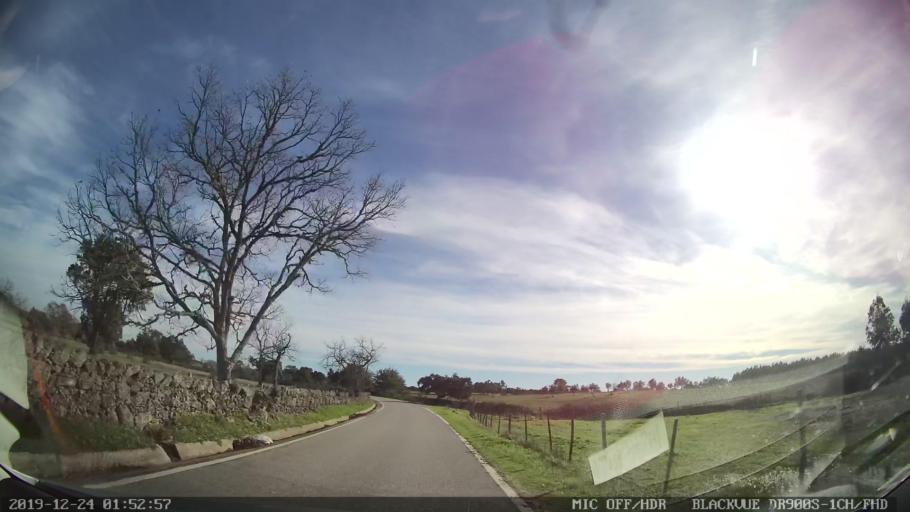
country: PT
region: Portalegre
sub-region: Nisa
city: Nisa
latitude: 39.4885
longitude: -7.7400
